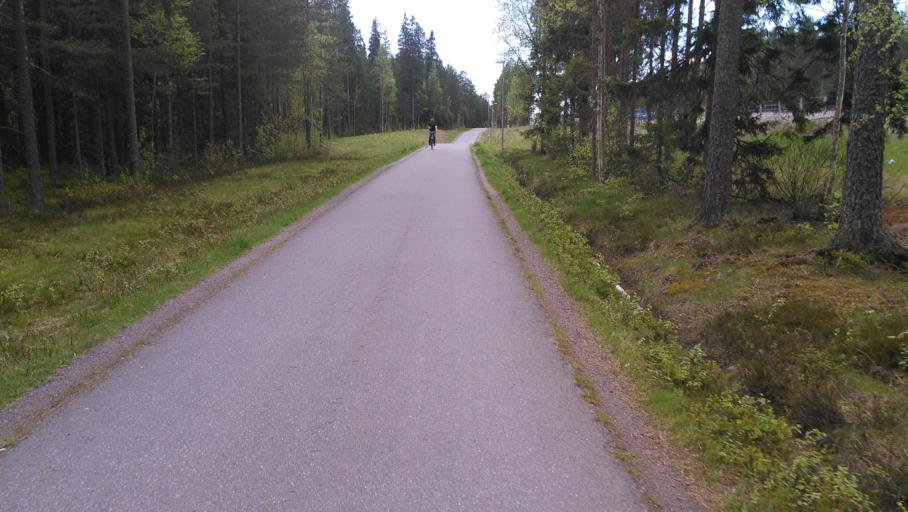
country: SE
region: Vaesterbotten
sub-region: Umea Kommun
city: Ersmark
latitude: 63.8236
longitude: 20.3312
